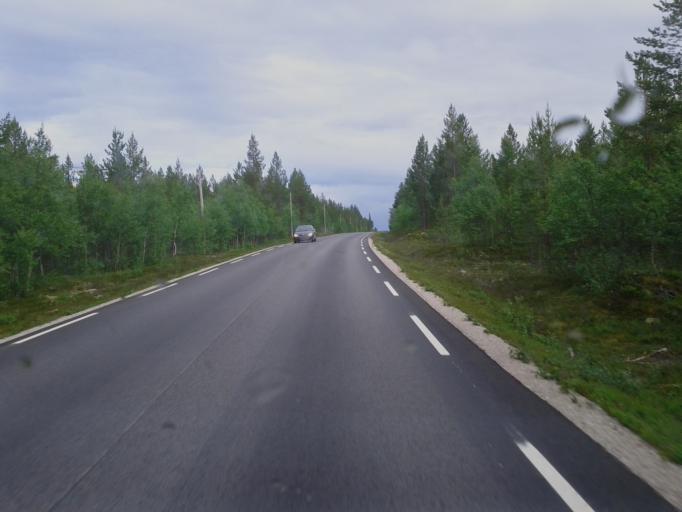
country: NO
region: Hedmark
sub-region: Engerdal
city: Engerdal
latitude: 62.0471
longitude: 11.6916
